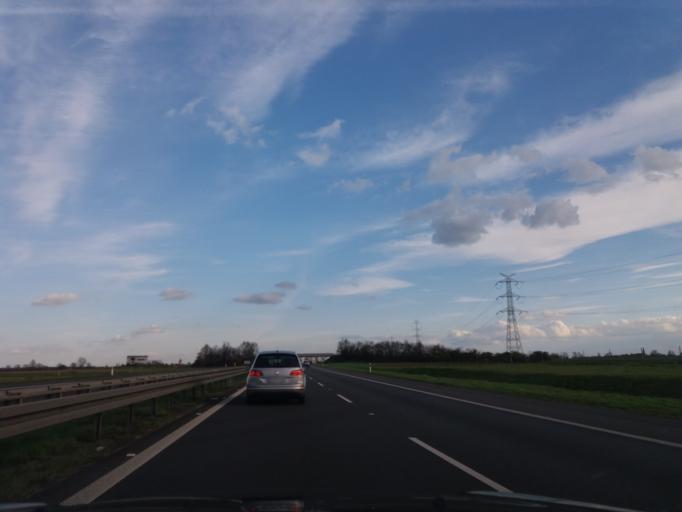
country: PL
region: Lower Silesian Voivodeship
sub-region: Powiat strzelinski
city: Wiazow
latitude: 50.8186
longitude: 17.3052
